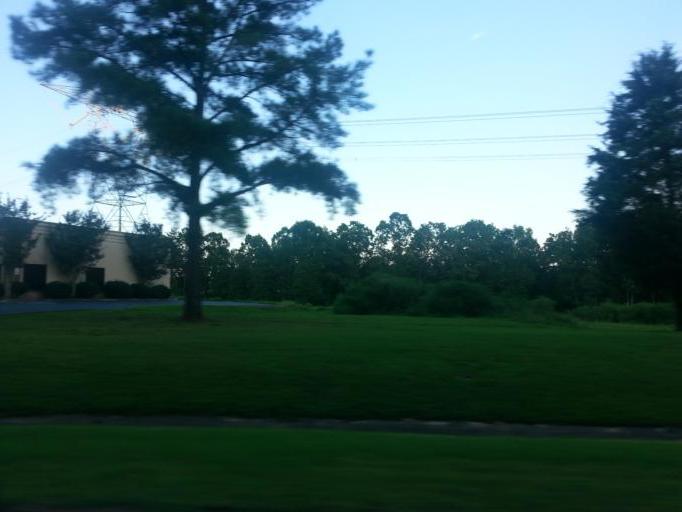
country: US
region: Tennessee
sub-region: Roane County
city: Midtown
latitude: 35.8288
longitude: -84.5458
